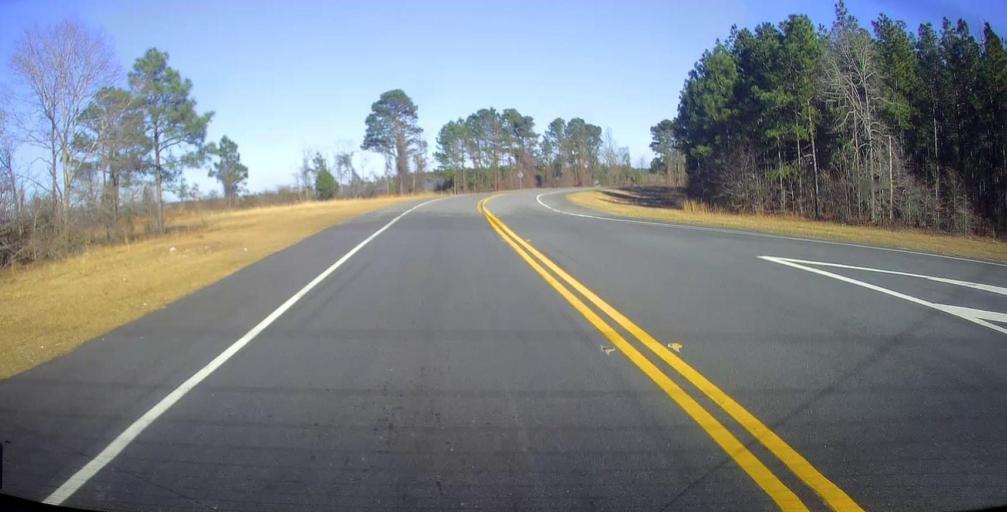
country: US
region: Georgia
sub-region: Taylor County
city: Butler
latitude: 32.5666
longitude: -84.2690
